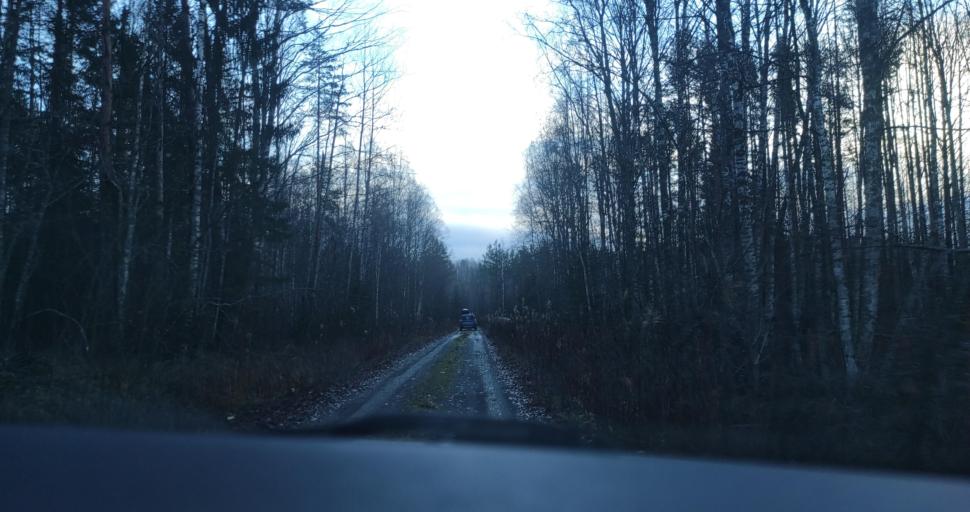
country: RU
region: Republic of Karelia
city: Pitkyaranta
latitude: 61.7330
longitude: 31.3764
